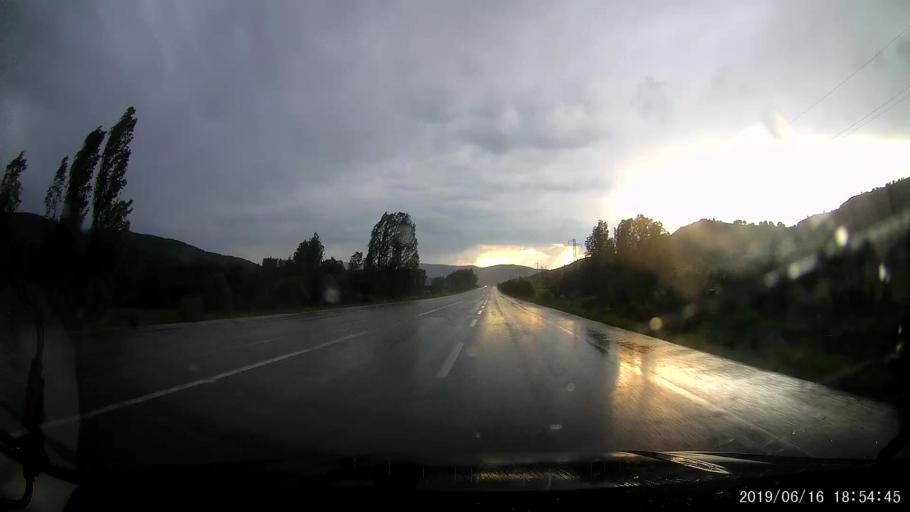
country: TR
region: Erzincan
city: Catalcam
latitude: 39.8977
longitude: 38.8458
